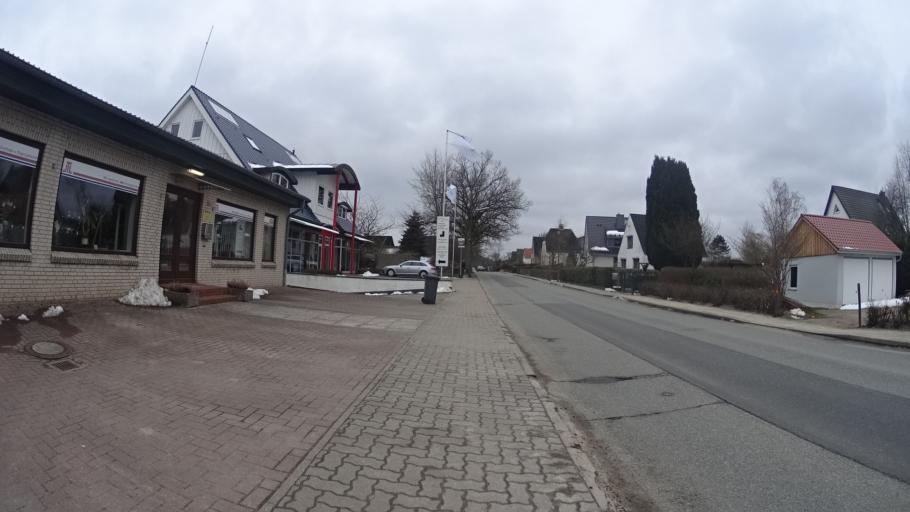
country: DE
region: Schleswig-Holstein
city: Malente
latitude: 54.1862
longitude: 10.5637
